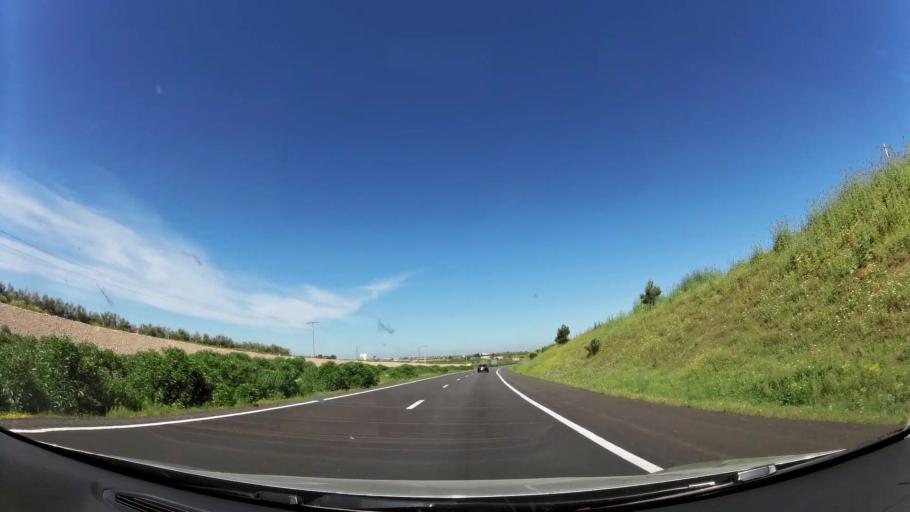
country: MA
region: Meknes-Tafilalet
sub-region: Meknes
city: Meknes
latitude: 33.8283
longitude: -5.5012
